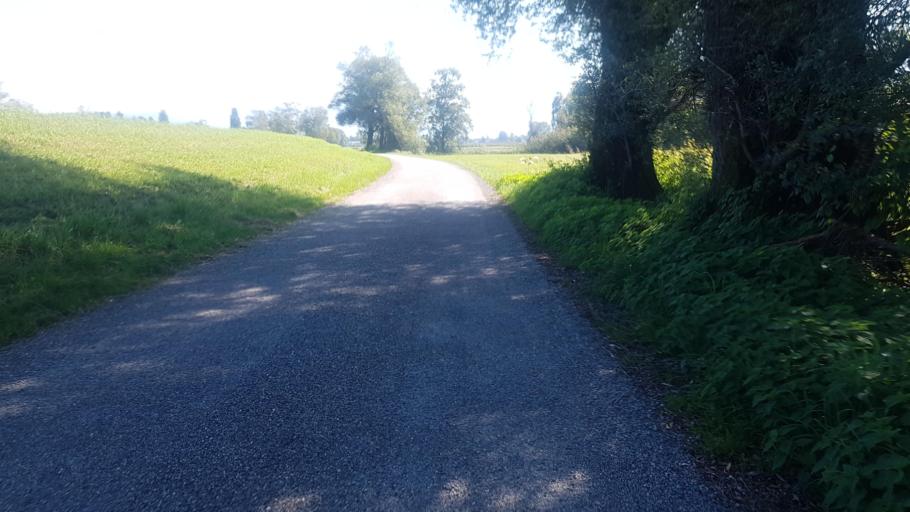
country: AT
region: Vorarlberg
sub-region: Politischer Bezirk Bregenz
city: Fussach
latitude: 47.4871
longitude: 9.6470
